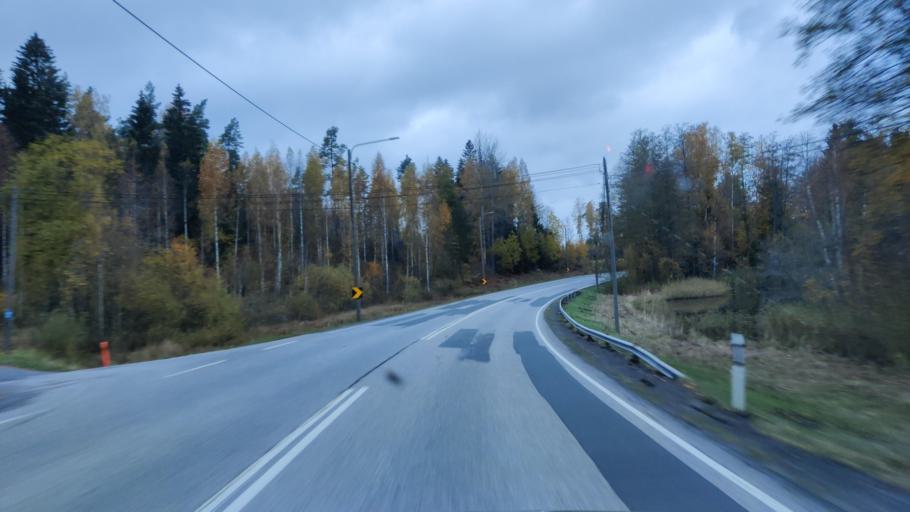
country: FI
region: Uusimaa
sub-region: Helsinki
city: Vihti
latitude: 60.3352
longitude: 24.2008
